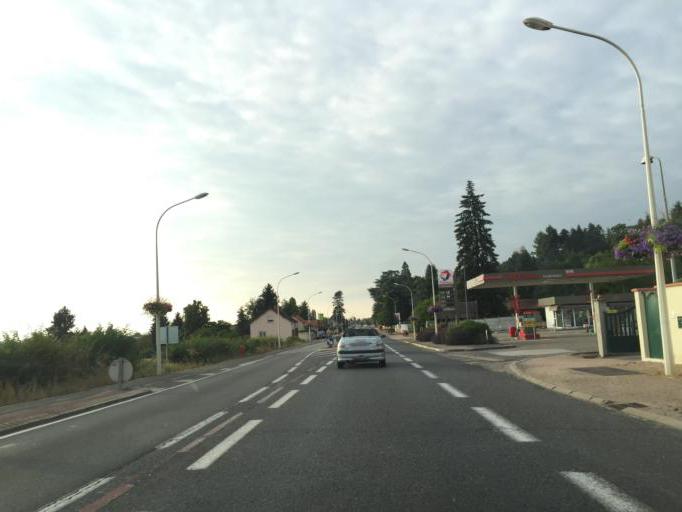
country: FR
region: Auvergne
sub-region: Departement de l'Allier
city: Varennes-sur-Allier
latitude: 46.3214
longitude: 3.3917
